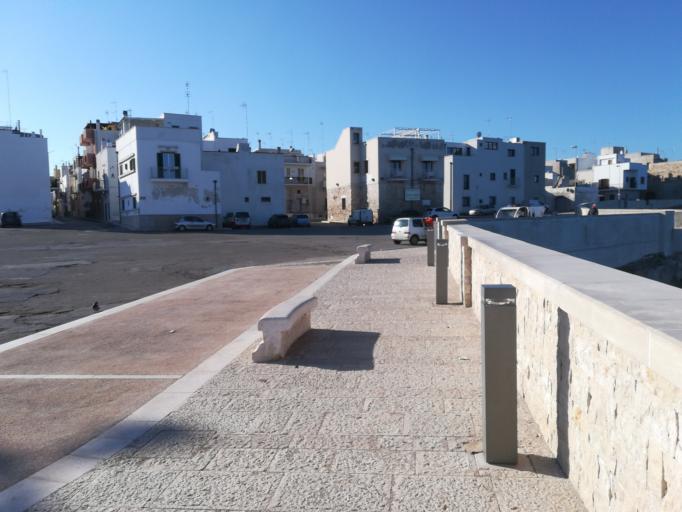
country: IT
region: Apulia
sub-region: Provincia di Bari
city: Polignano a Mare
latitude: 40.9969
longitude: 17.2236
